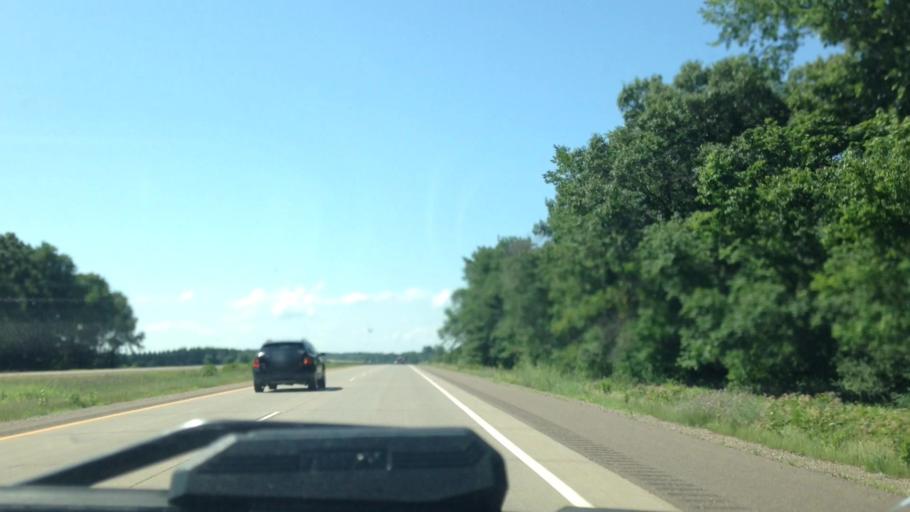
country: US
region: Wisconsin
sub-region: Barron County
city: Cameron
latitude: 45.4283
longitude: -91.7625
